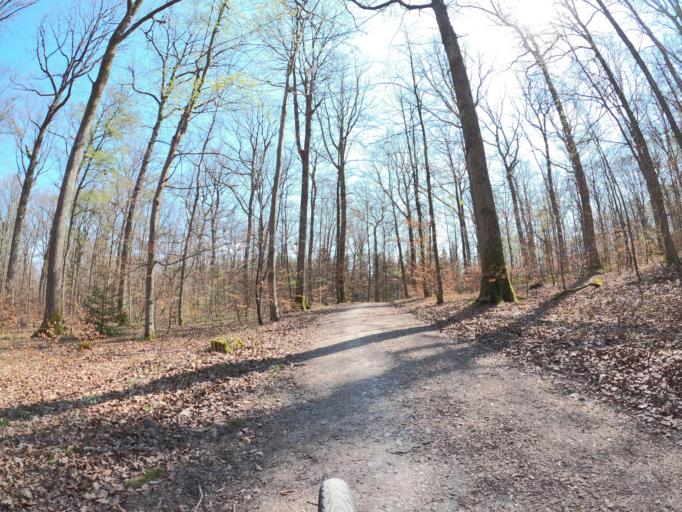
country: DE
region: Baden-Wuerttemberg
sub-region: Tuebingen Region
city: Wannweil
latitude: 48.4710
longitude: 9.1471
